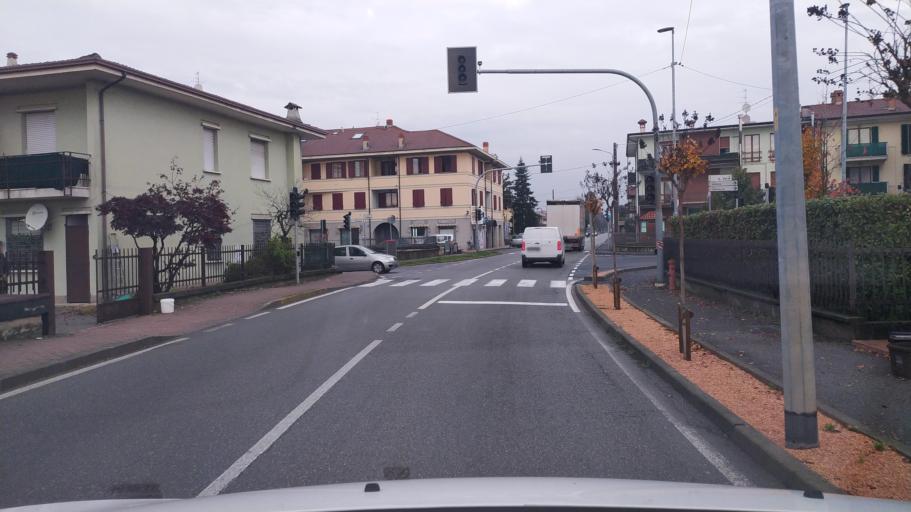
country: IT
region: Lombardy
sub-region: Provincia di Brescia
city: Pontoglio
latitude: 45.5674
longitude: 9.8576
